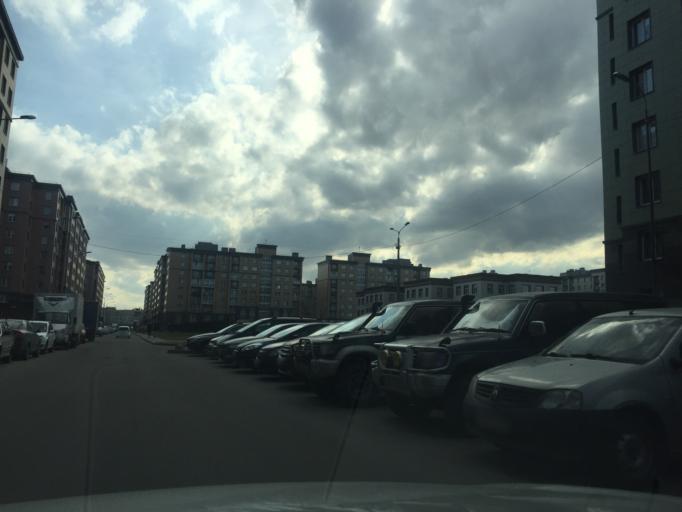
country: RU
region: St.-Petersburg
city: Tyarlevo
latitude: 59.7391
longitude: 30.4752
